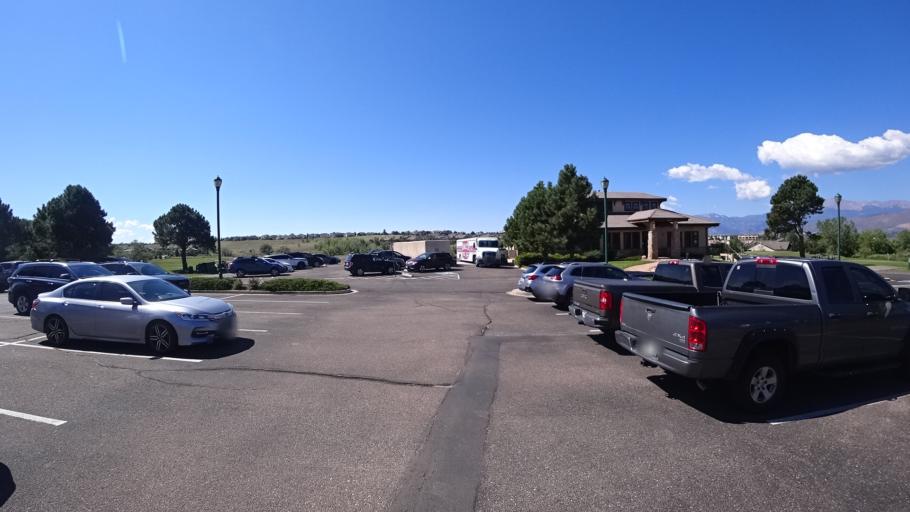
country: US
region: Colorado
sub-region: El Paso County
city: Black Forest
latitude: 38.9731
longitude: -104.7759
